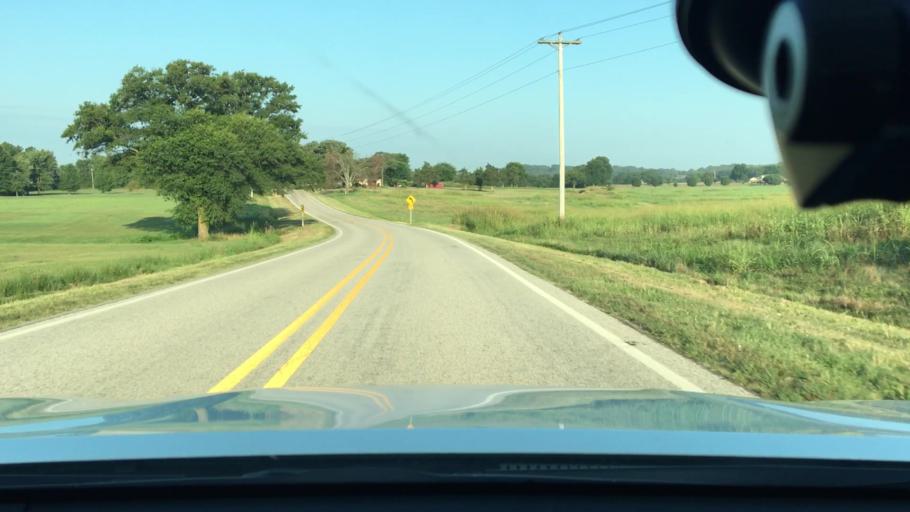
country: US
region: Arkansas
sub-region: Johnson County
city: Coal Hill
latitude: 35.3475
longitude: -93.5902
